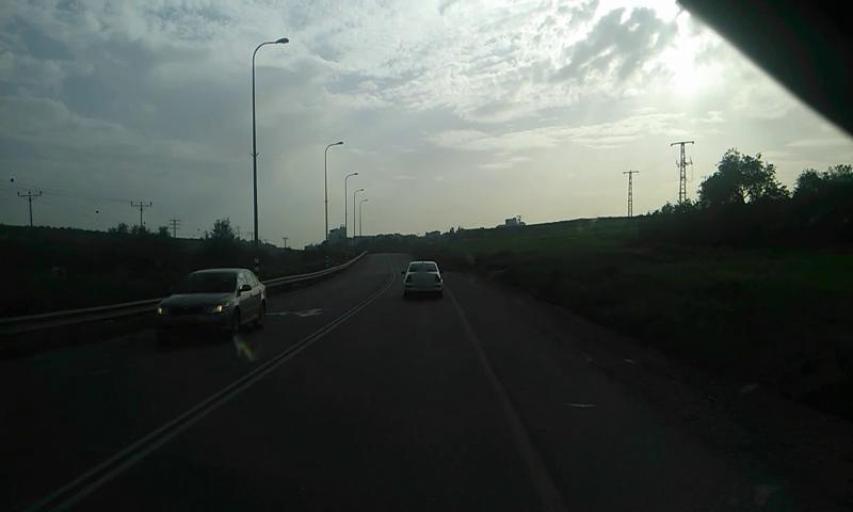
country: PS
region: West Bank
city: Immatin
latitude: 32.1958
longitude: 35.1437
